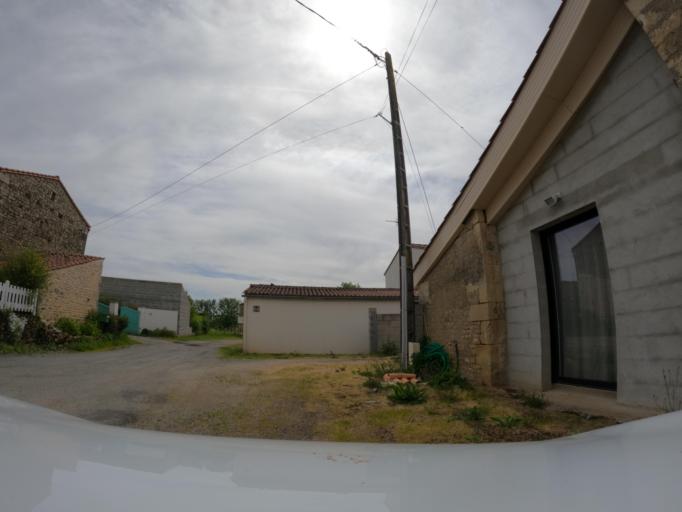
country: FR
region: Pays de la Loire
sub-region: Departement de la Vendee
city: Saint-Hilaire-des-Loges
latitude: 46.4892
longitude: -0.6312
